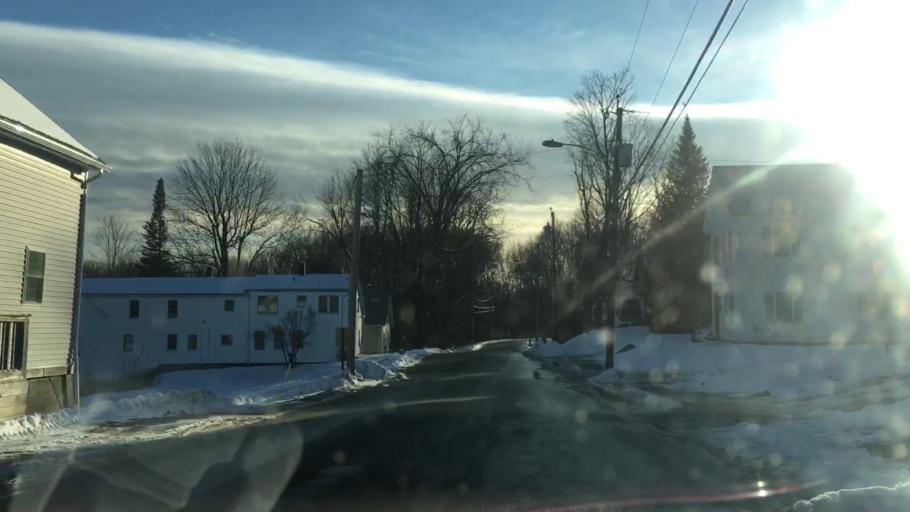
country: US
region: Maine
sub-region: Kennebec County
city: Gardiner
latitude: 44.2297
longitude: -69.7829
